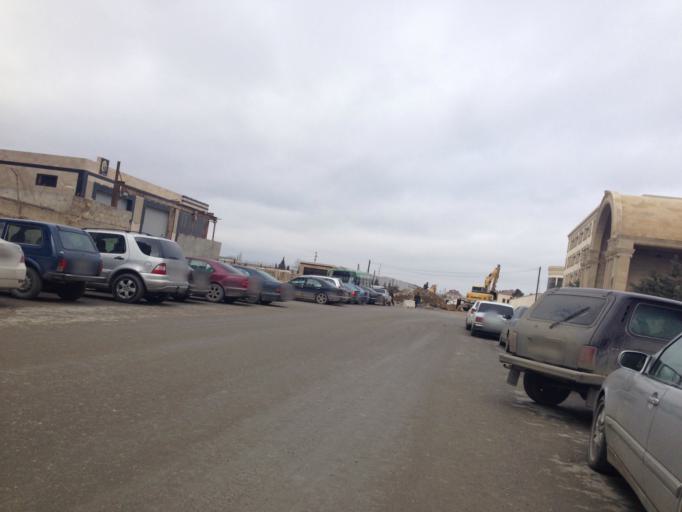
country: AZ
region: Baki
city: Sabuncu
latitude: 40.4193
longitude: 49.9100
